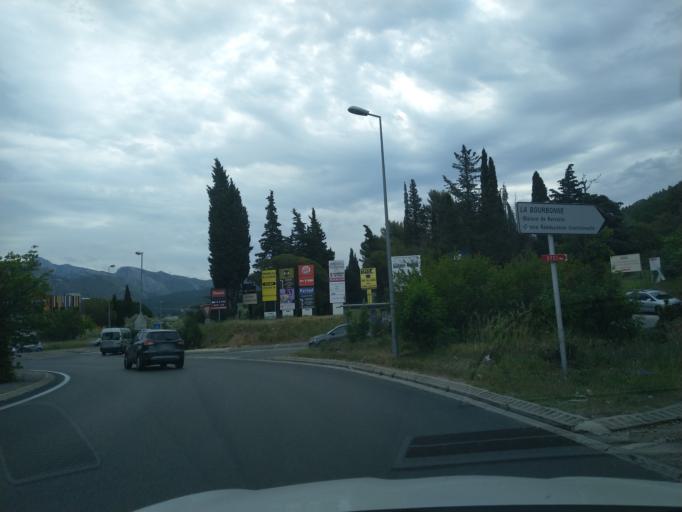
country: FR
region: Provence-Alpes-Cote d'Azur
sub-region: Departement des Bouches-du-Rhone
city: Aubagne
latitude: 43.2836
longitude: 5.5940
